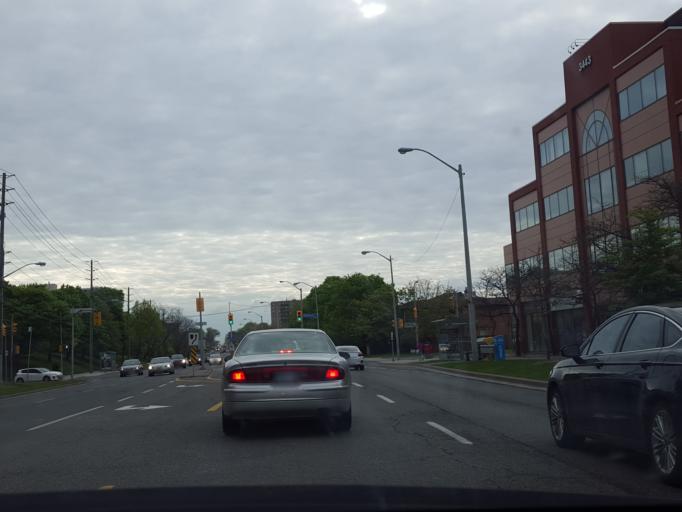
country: CA
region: Ontario
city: Scarborough
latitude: 43.7973
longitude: -79.3134
